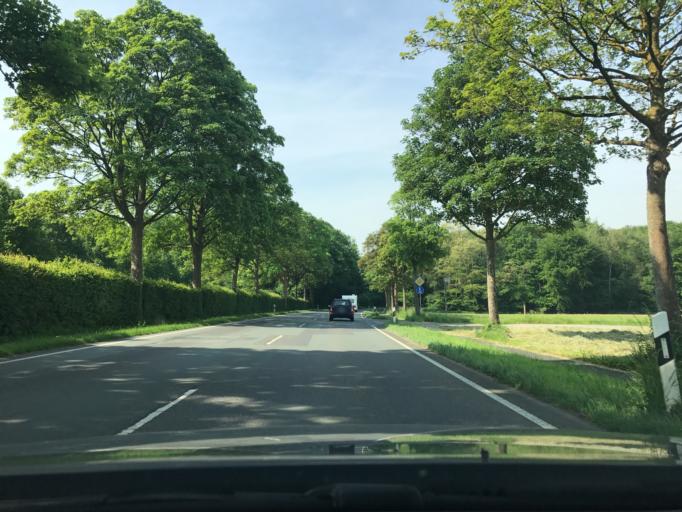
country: DE
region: North Rhine-Westphalia
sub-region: Regierungsbezirk Dusseldorf
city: Wachtendonk
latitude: 51.4198
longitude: 6.3622
